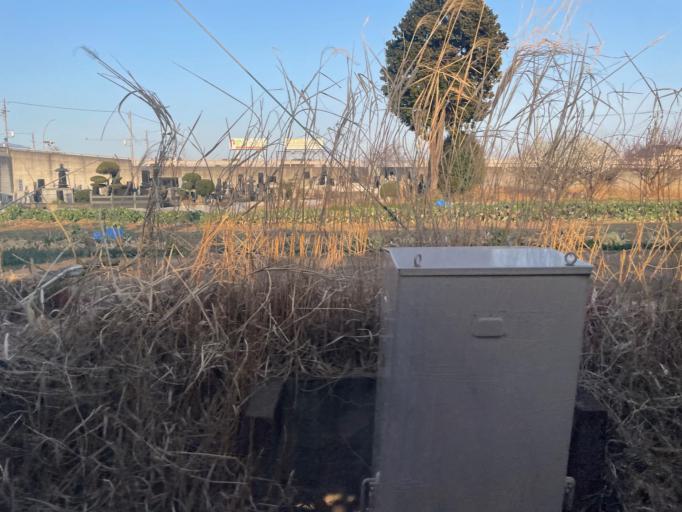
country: JP
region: Gunma
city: Kanekomachi
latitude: 36.4275
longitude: 139.0299
